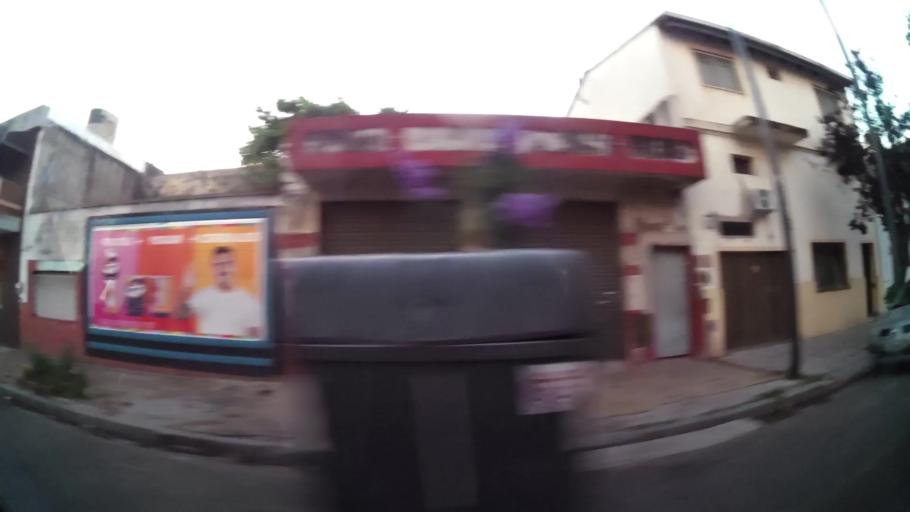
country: AR
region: Buenos Aires F.D.
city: Villa Lugano
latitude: -34.6418
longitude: -58.4349
